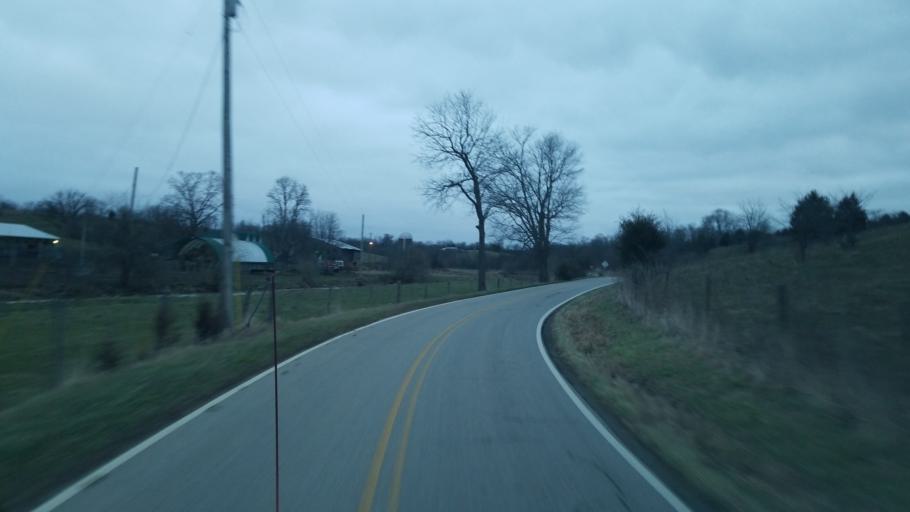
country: US
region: Kentucky
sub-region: Fleming County
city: Flemingsburg
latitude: 38.5142
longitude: -83.7015
